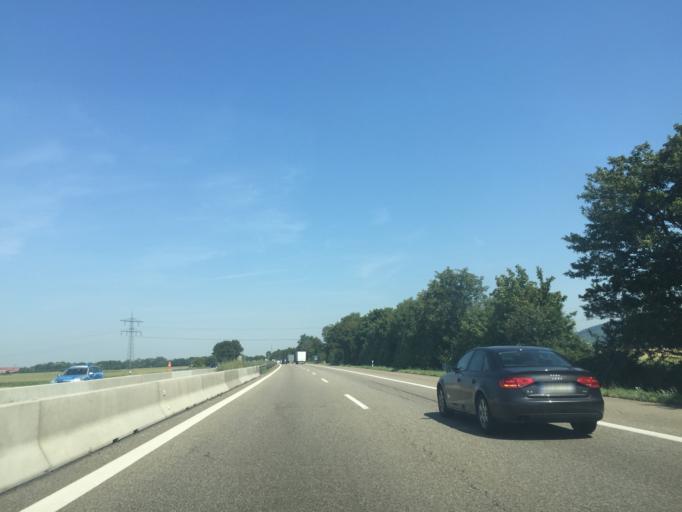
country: DE
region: Baden-Wuerttemberg
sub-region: Karlsruhe Region
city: Schriesheim
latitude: 49.4569
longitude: 8.6467
